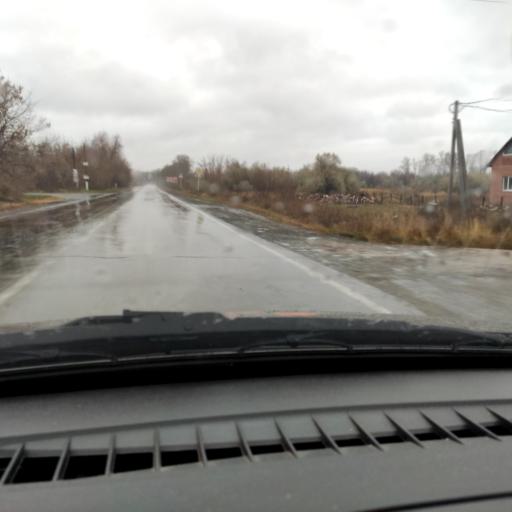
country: RU
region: Samara
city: Tol'yatti
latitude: 53.6513
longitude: 49.2914
